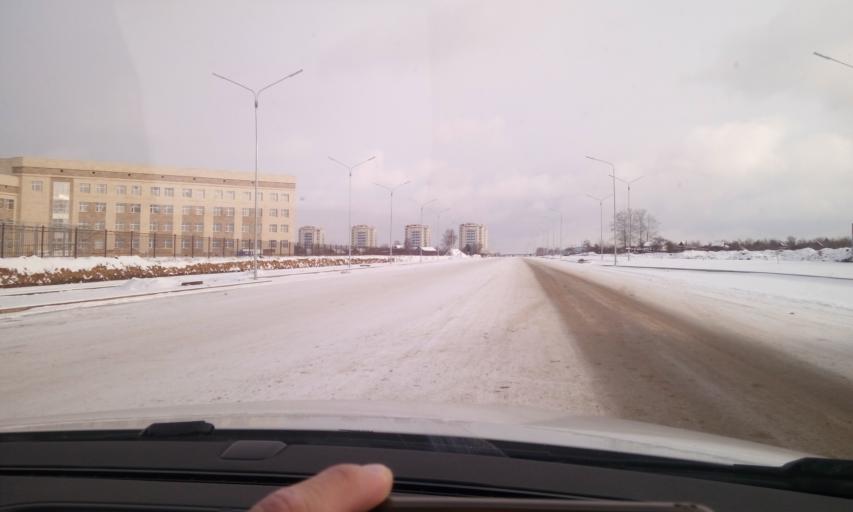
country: KZ
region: Astana Qalasy
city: Astana
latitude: 51.1209
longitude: 71.4934
